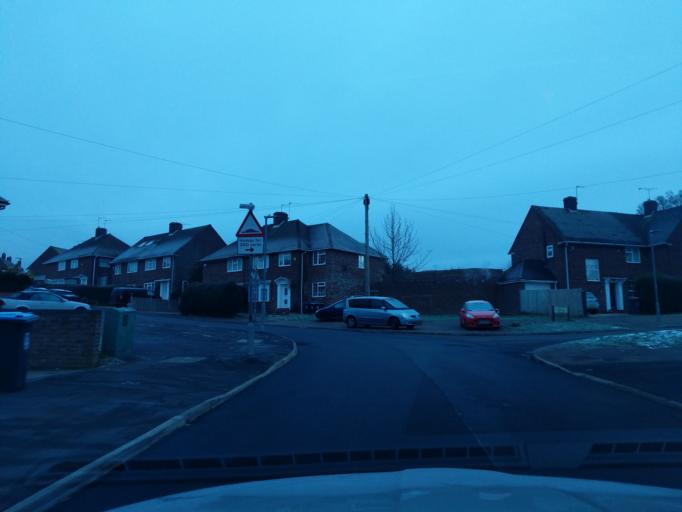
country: GB
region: England
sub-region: Hertfordshire
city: Hemel Hempstead
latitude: 51.7379
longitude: -0.4579
